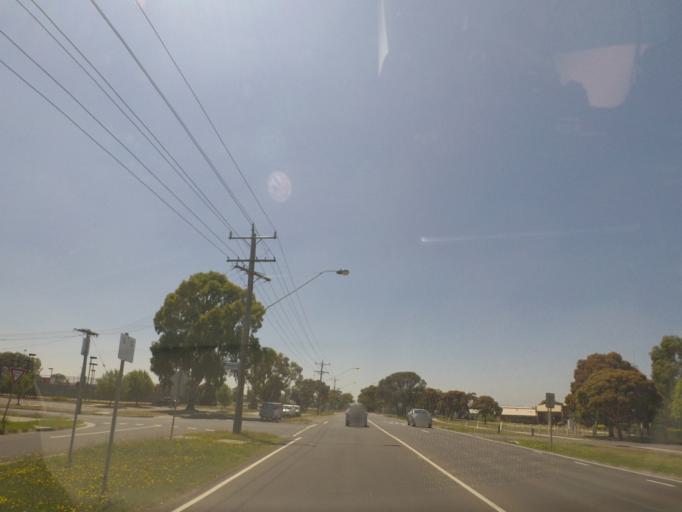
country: AU
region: Victoria
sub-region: Hume
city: Craigieburn
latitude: -37.5978
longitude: 144.9311
